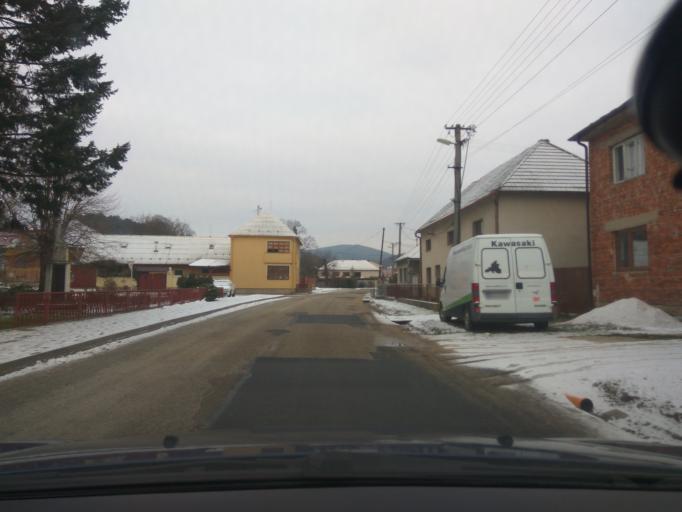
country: SK
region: Nitriansky
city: Stara Tura
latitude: 48.7851
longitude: 17.7352
